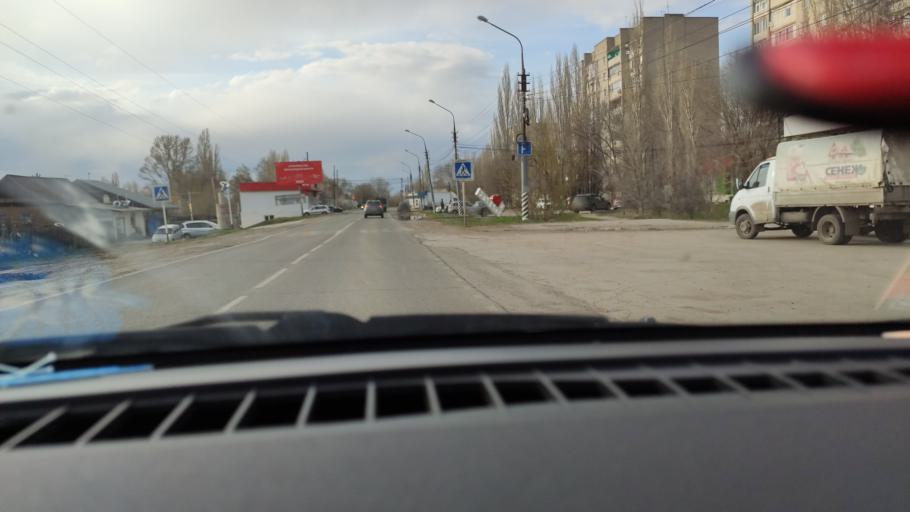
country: RU
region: Saratov
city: Privolzhskiy
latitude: 51.3909
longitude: 46.0353
